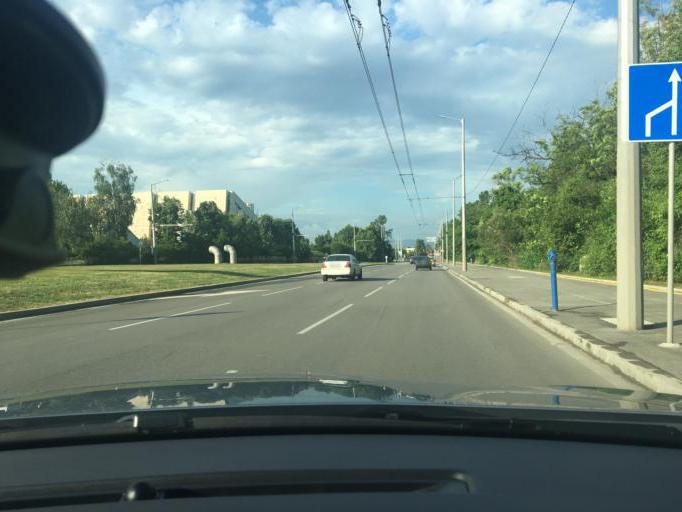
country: BG
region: Sofia-Capital
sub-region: Stolichna Obshtina
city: Sofia
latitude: 42.6723
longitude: 23.3725
